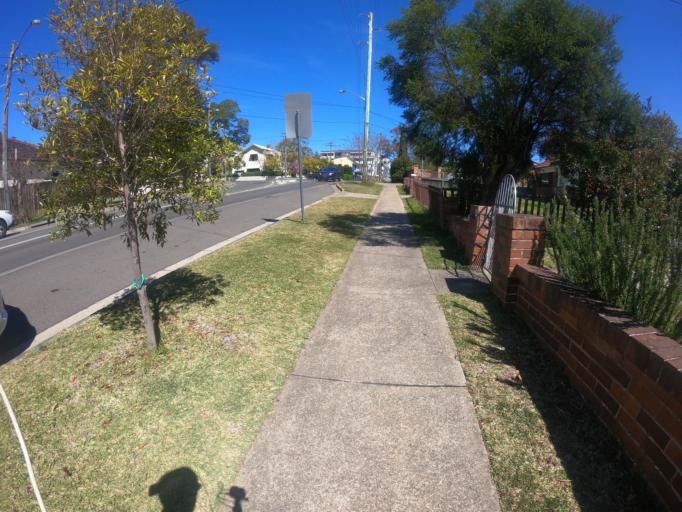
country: AU
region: New South Wales
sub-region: Ryde
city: East Ryde
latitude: -33.8221
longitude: 151.1255
